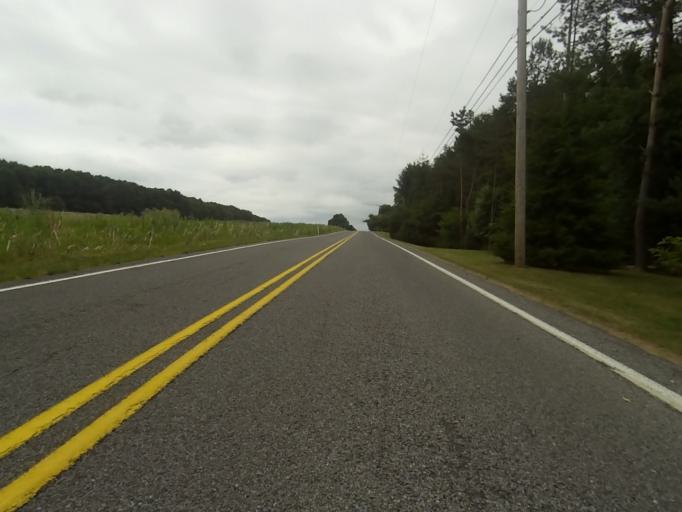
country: US
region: Pennsylvania
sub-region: Centre County
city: Stormstown
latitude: 40.7147
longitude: -78.0055
